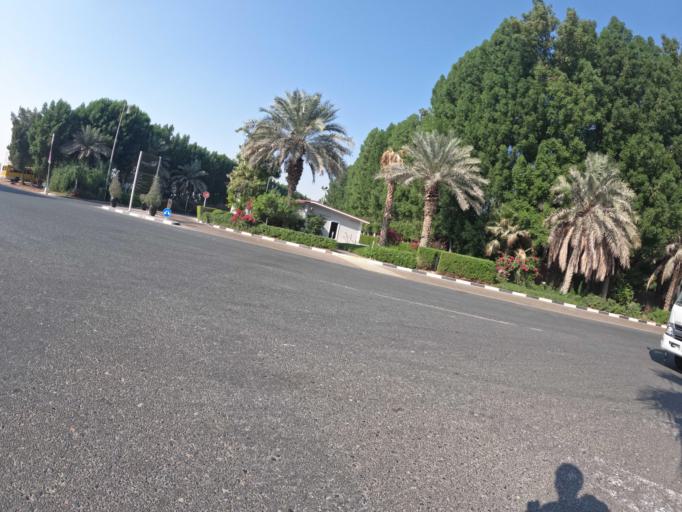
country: AE
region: Dubai
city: Dubai
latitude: 25.0932
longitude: 55.3104
